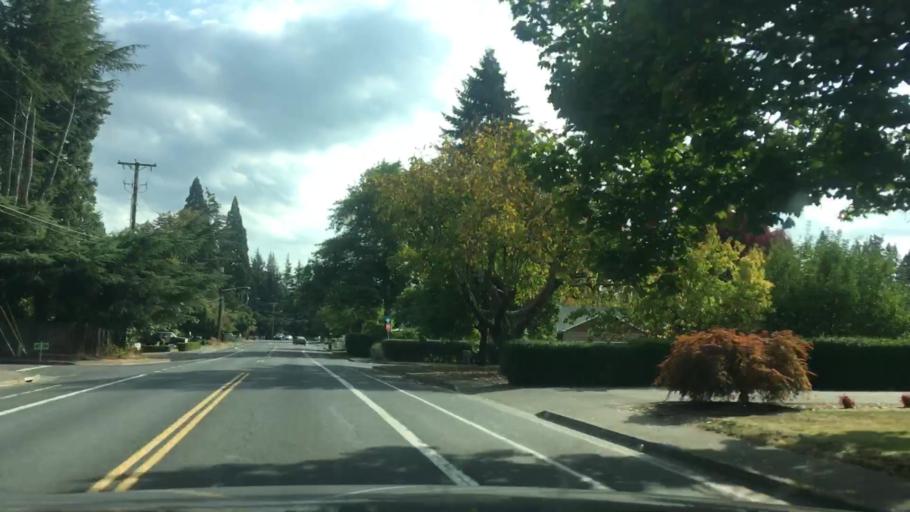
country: US
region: Oregon
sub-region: Lane County
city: Eugene
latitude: 44.0854
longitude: -123.0881
